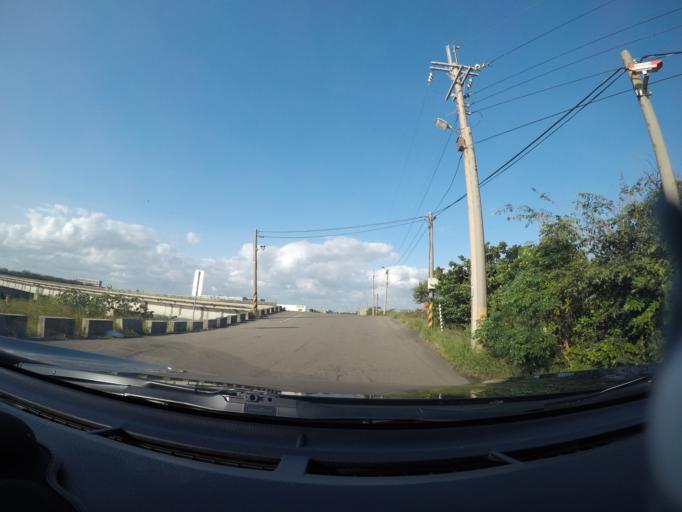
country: TW
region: Taiwan
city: Taoyuan City
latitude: 25.1015
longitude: 121.2518
